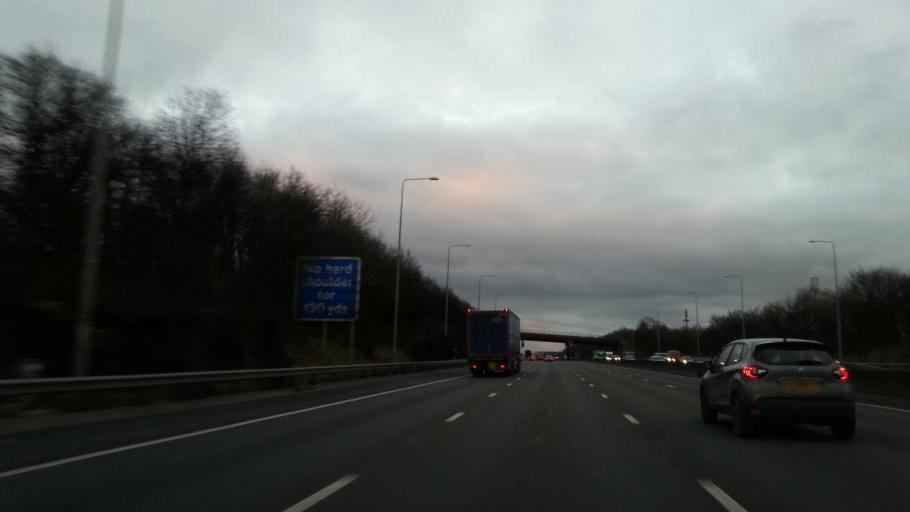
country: GB
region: England
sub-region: Derbyshire
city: Pinxton
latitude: 53.0828
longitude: -1.2976
